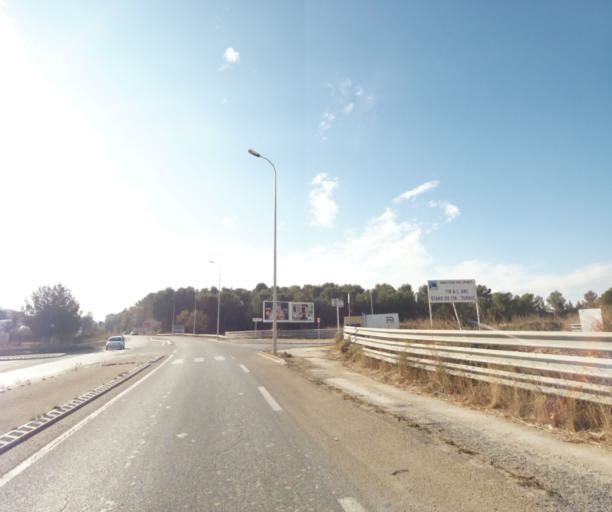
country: FR
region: Provence-Alpes-Cote d'Azur
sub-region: Departement des Bouches-du-Rhone
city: Allauch
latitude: 43.3207
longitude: 5.4685
